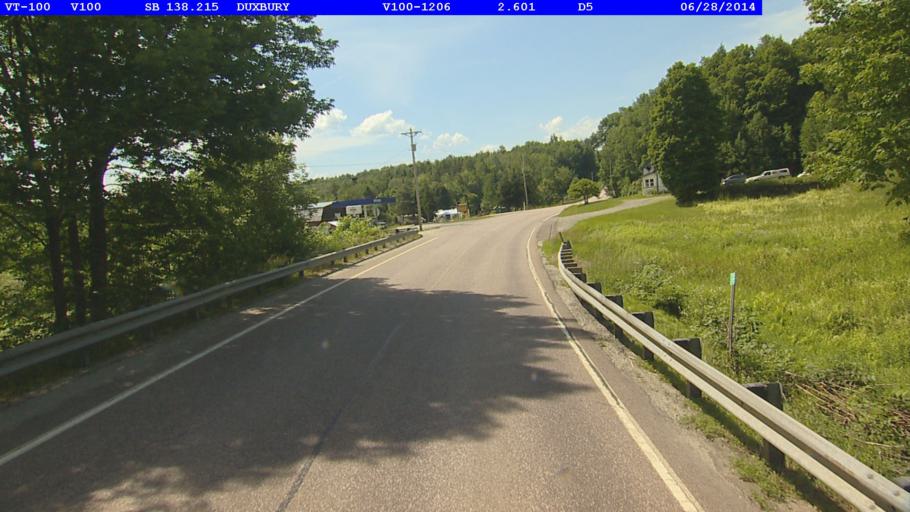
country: US
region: Vermont
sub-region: Washington County
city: Waterbury
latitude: 44.2831
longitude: -72.7822
